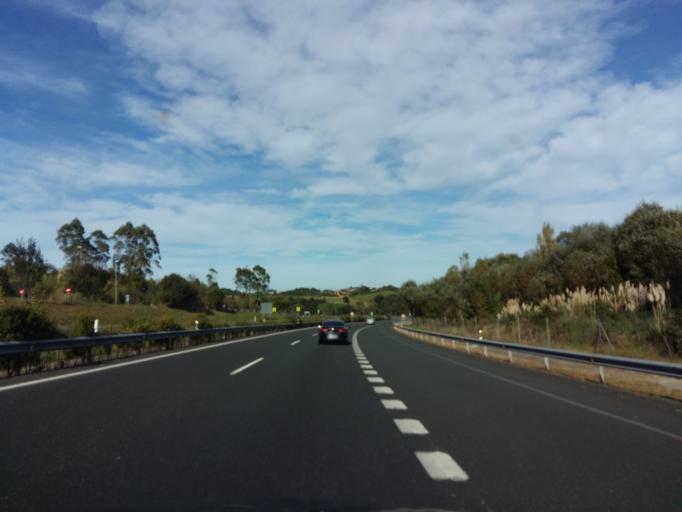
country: ES
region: Cantabria
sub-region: Provincia de Cantabria
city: Comillas
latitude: 43.3349
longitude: -4.3314
